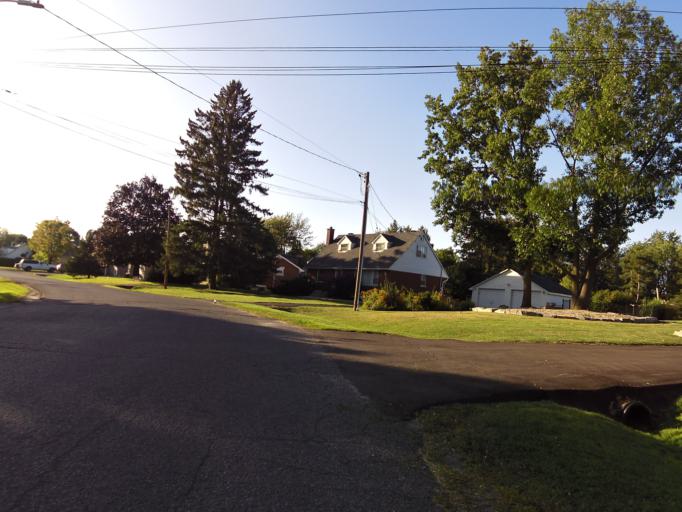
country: CA
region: Ontario
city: Ottawa
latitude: 45.3536
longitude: -75.7177
